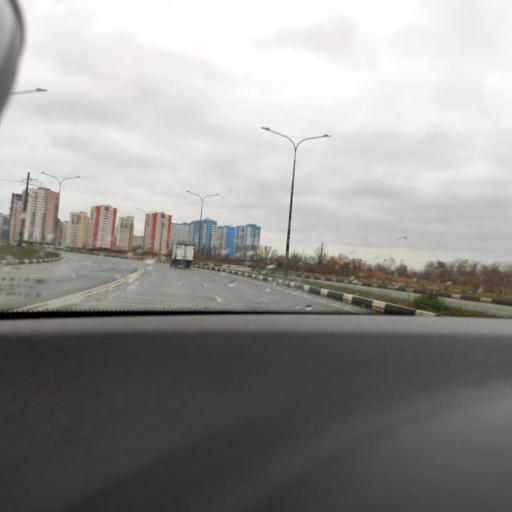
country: RU
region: Samara
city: Samara
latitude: 53.1410
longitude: 50.0780
